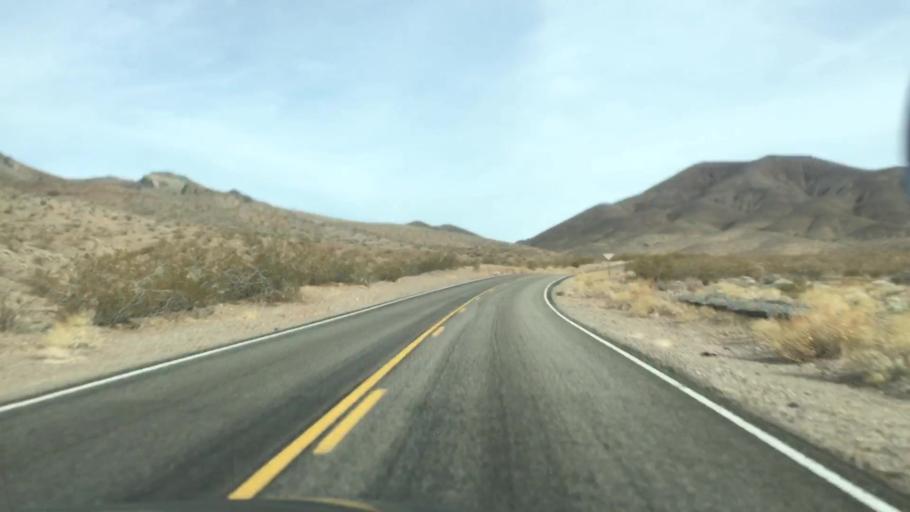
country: US
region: Nevada
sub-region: Nye County
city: Beatty
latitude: 36.7548
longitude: -116.9347
